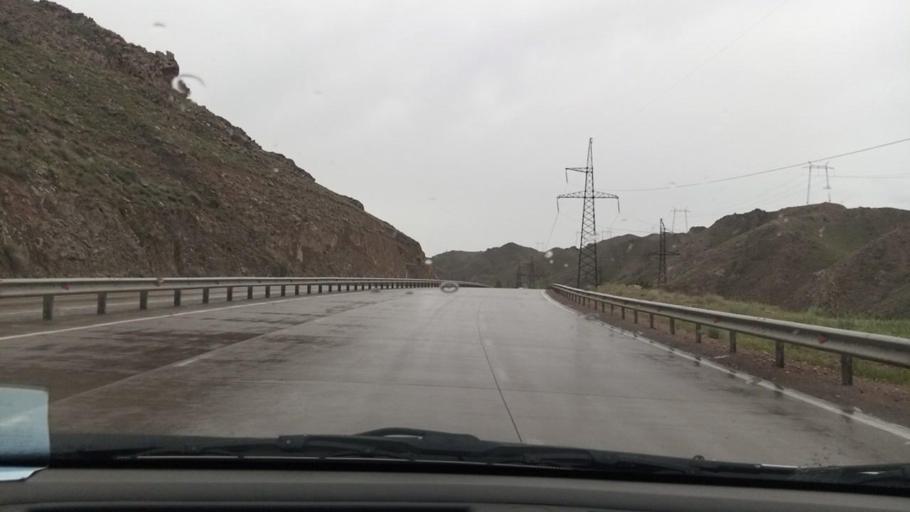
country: TJ
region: Viloyati Sughd
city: Shaydon
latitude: 40.9729
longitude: 70.6531
